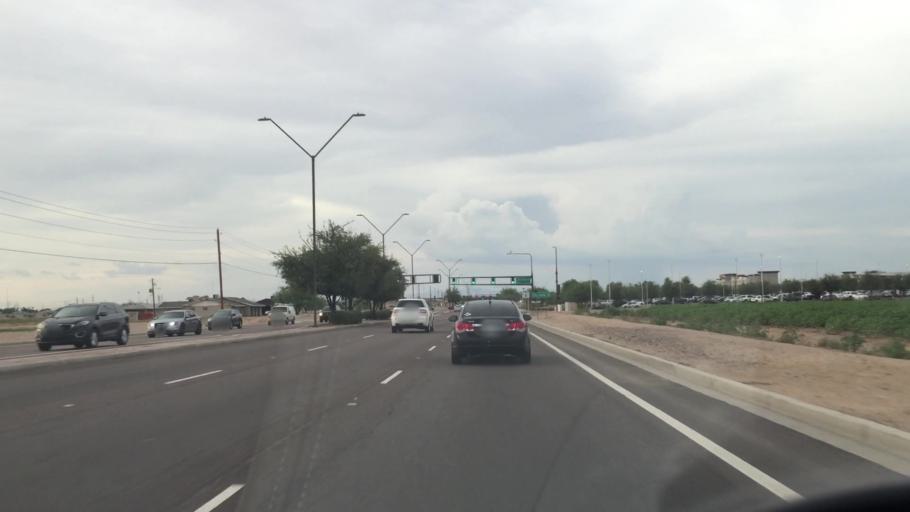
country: US
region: Arizona
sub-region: Maricopa County
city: Avondale
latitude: 33.4507
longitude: -112.3065
